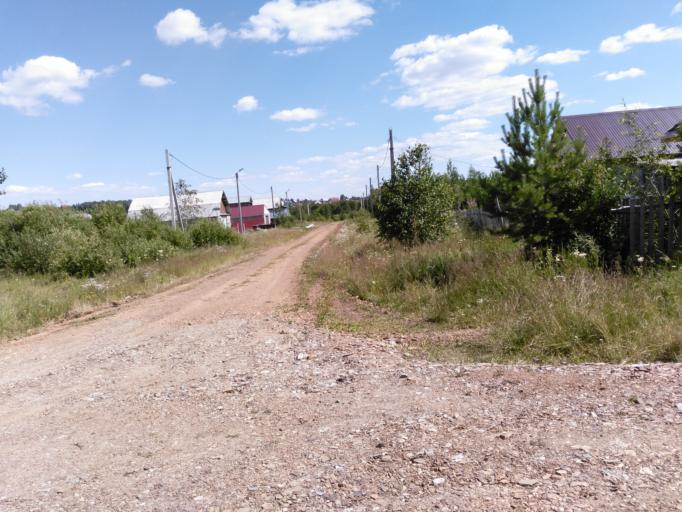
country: RU
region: Bashkortostan
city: Uchaly
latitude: 54.2885
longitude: 59.3569
